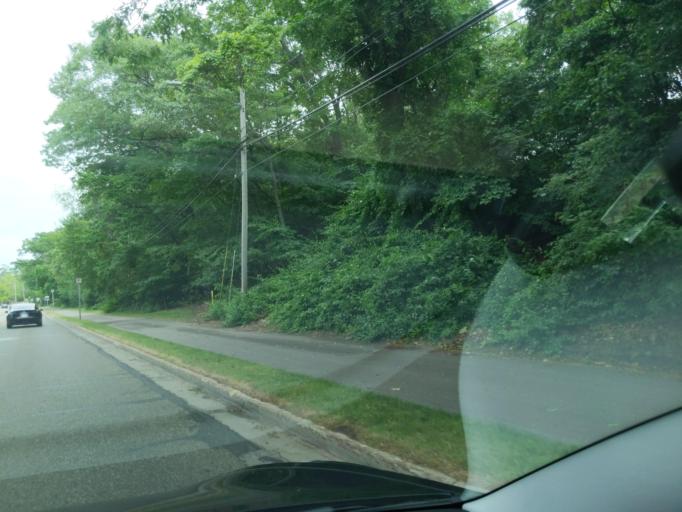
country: US
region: Michigan
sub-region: Muskegon County
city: Roosevelt Park
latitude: 43.2143
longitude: -86.3105
